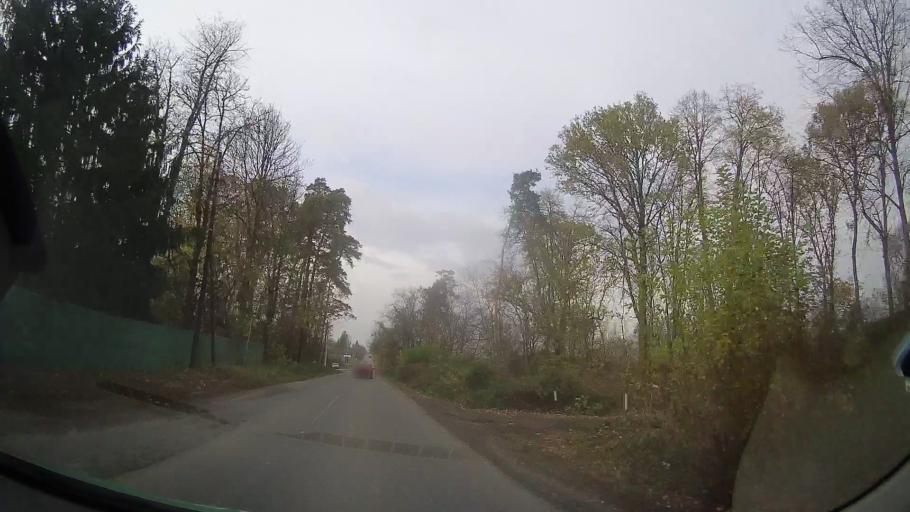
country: RO
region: Prahova
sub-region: Comuna Gorgota
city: Potigrafu
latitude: 44.7704
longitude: 26.1097
